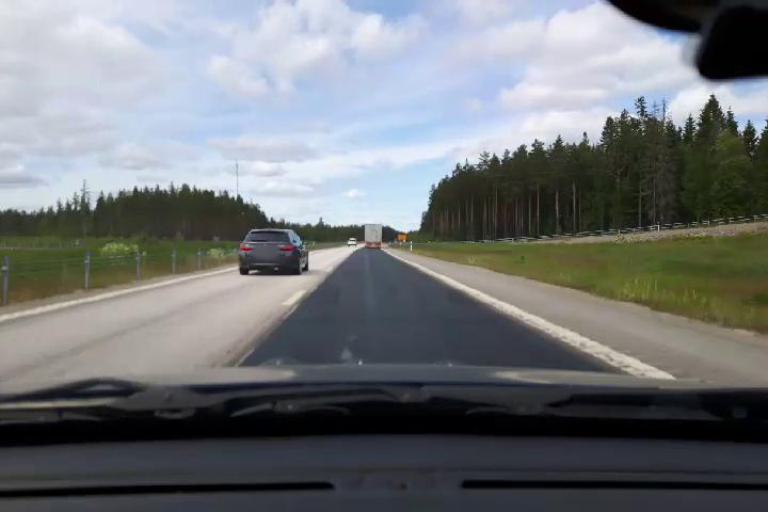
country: SE
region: Uppsala
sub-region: Alvkarleby Kommun
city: AElvkarleby
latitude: 60.4398
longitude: 17.4208
